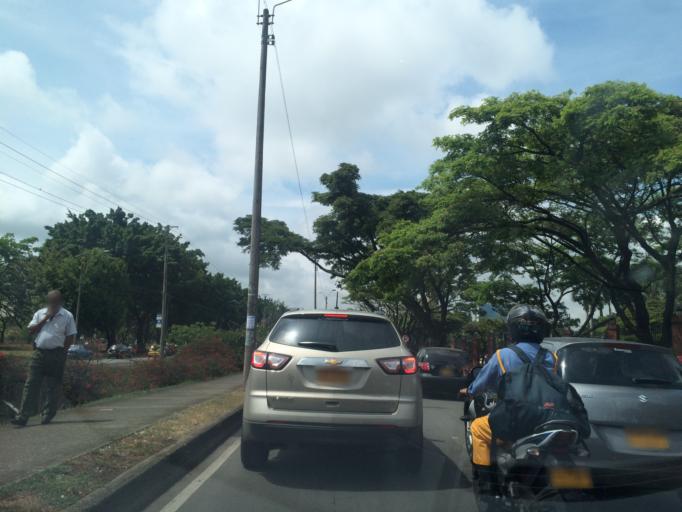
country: CO
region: Valle del Cauca
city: Cali
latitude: 3.3726
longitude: -76.5255
